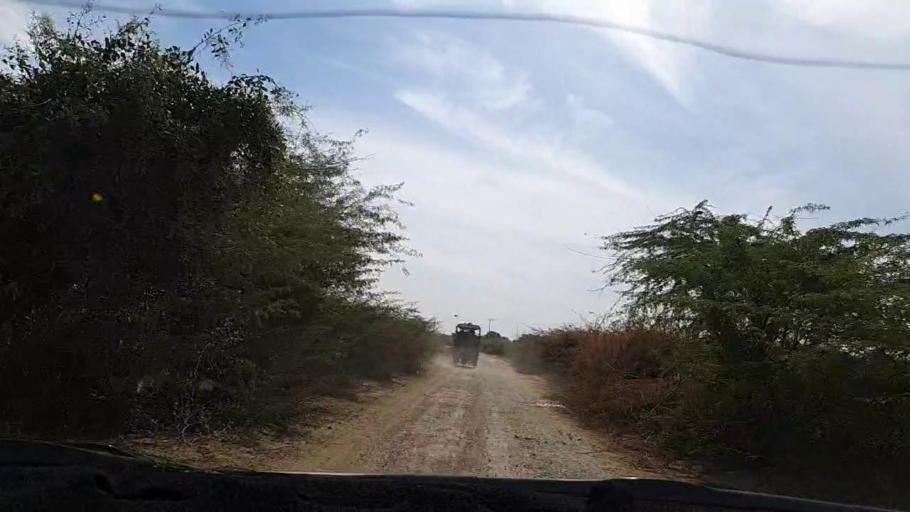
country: PK
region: Sindh
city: Pithoro
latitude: 25.4647
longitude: 69.4555
